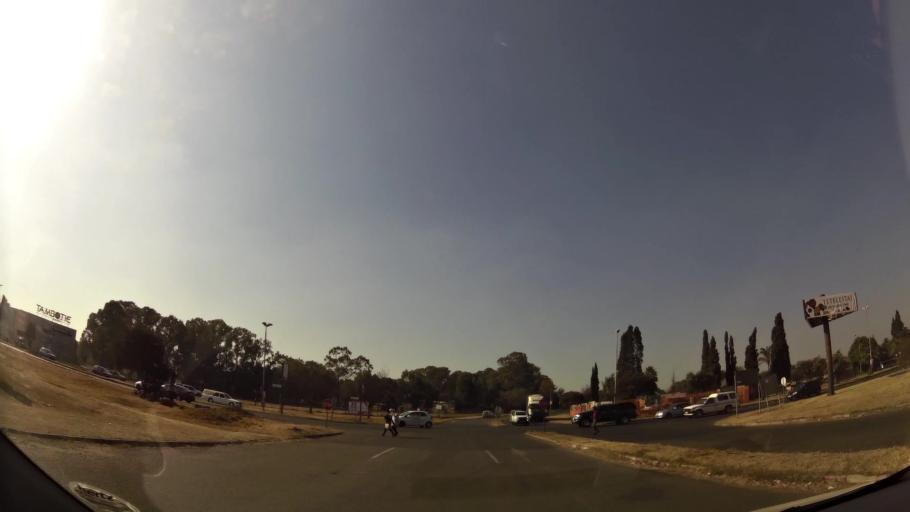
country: ZA
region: Gauteng
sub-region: West Rand District Municipality
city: Randfontein
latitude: -26.1746
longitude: 27.6944
